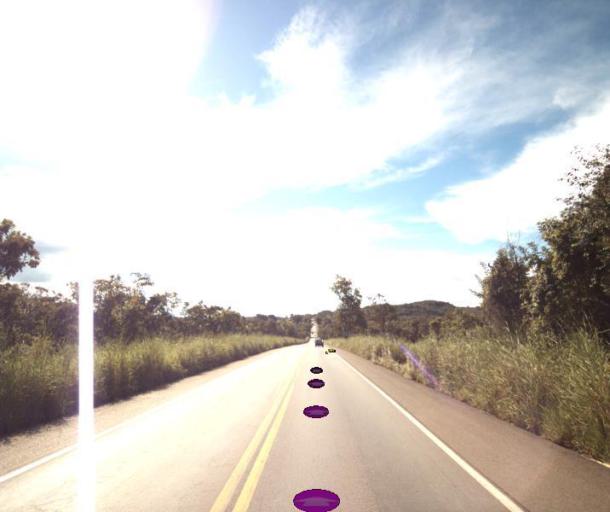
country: BR
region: Goias
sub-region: Uruana
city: Uruana
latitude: -15.5197
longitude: -49.4683
